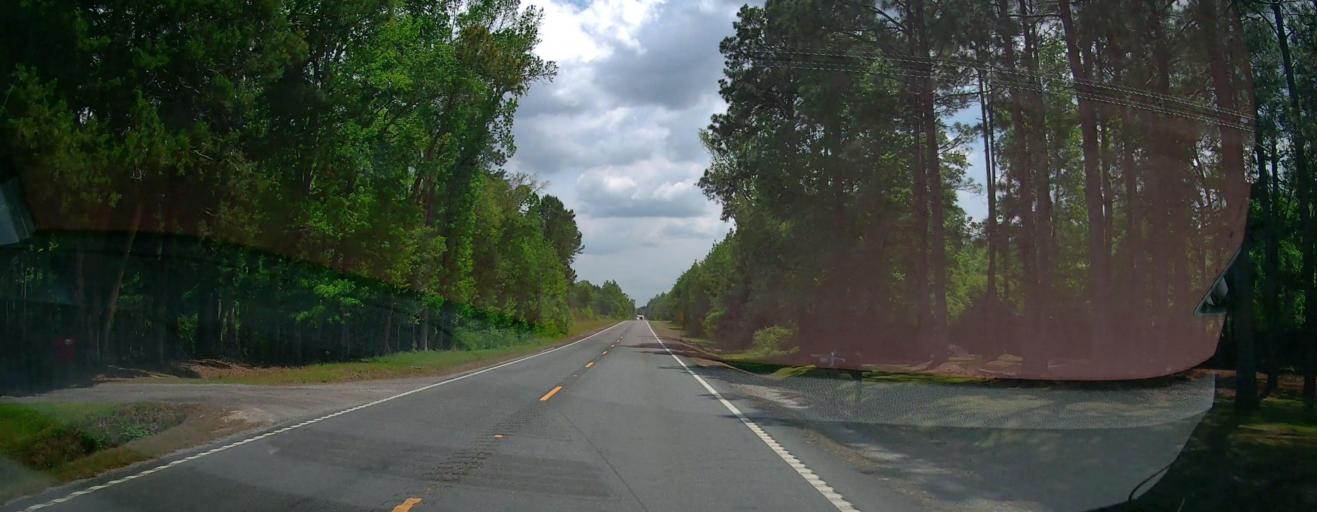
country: US
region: Georgia
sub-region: Treutlen County
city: Soperton
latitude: 32.3966
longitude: -82.6025
